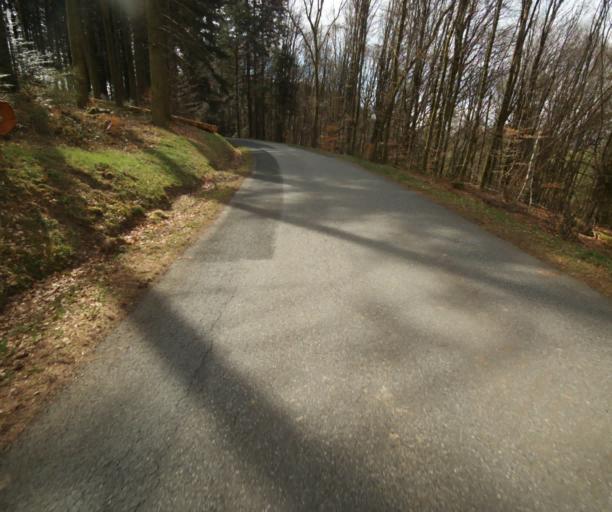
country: FR
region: Limousin
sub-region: Departement de la Correze
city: Correze
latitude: 45.3733
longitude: 1.9021
